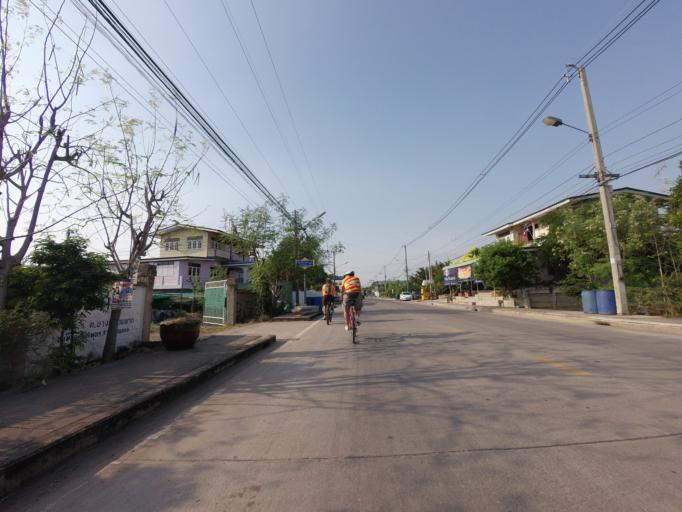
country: TH
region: Samut Sakhon
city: Samut Sakhon
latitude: 13.5219
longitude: 100.2742
